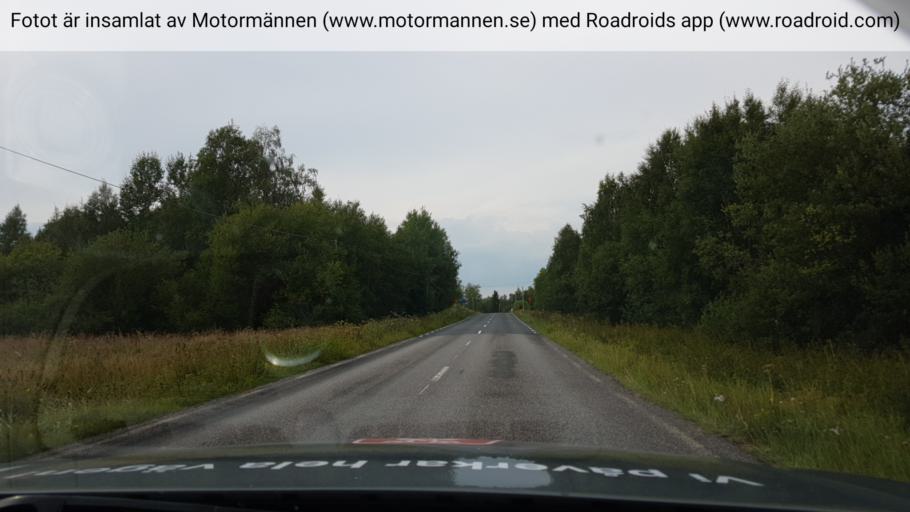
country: SE
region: Jaemtland
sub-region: Ragunda Kommun
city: Hammarstrand
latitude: 63.0067
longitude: 16.0760
